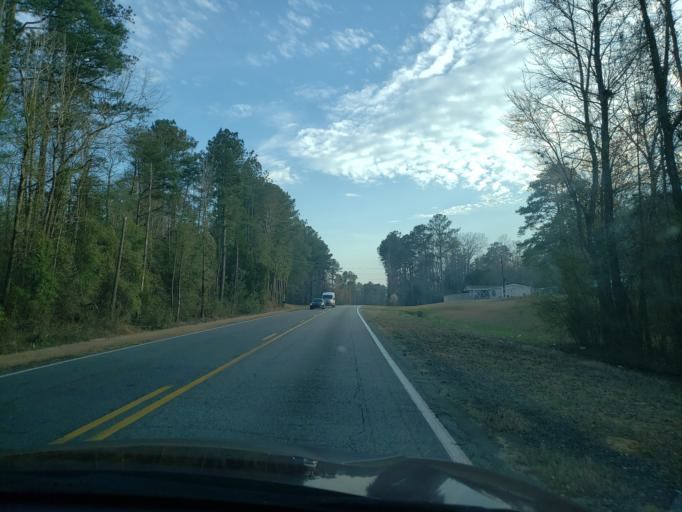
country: US
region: Alabama
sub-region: Hale County
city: Greensboro
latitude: 32.7356
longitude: -87.5861
